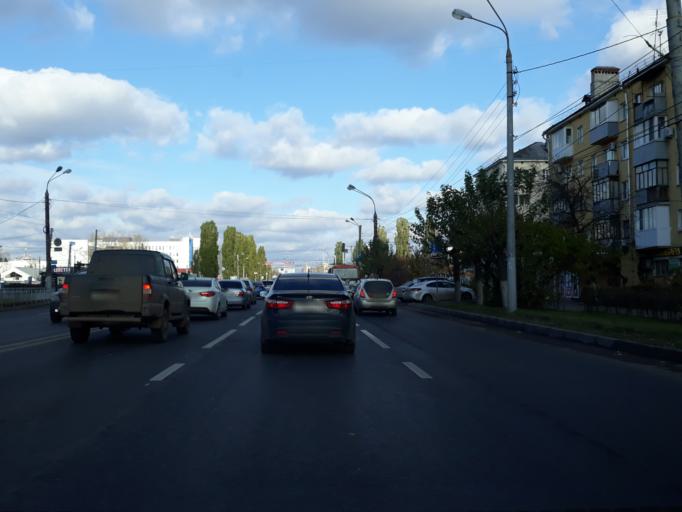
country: RU
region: Nizjnij Novgorod
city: Nizhniy Novgorod
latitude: 56.2831
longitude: 43.9265
